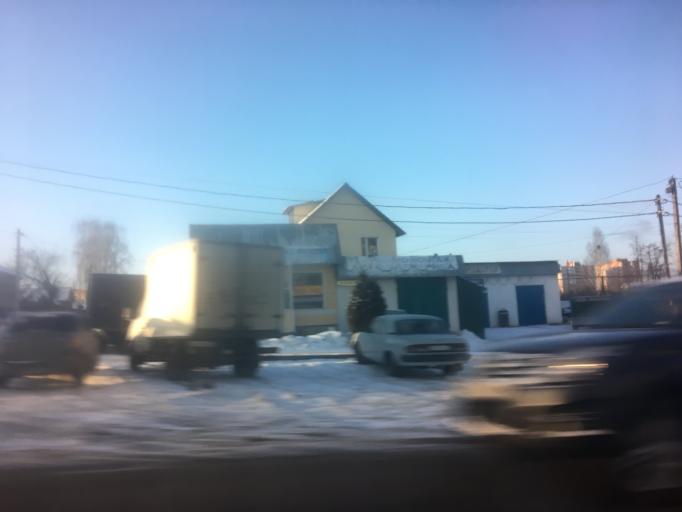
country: RU
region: Tula
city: Tula
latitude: 54.2023
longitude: 37.6809
